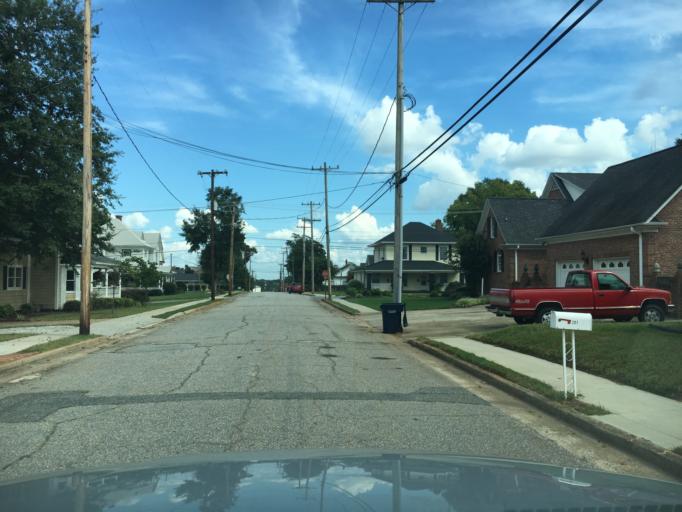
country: US
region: South Carolina
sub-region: Greenville County
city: Greer
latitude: 34.9411
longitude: -82.2293
